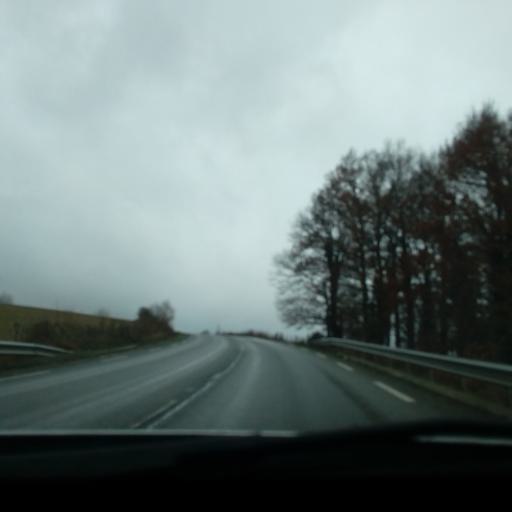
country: FR
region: Limousin
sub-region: Departement de la Creuse
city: Gueret
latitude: 46.1797
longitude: 1.8956
